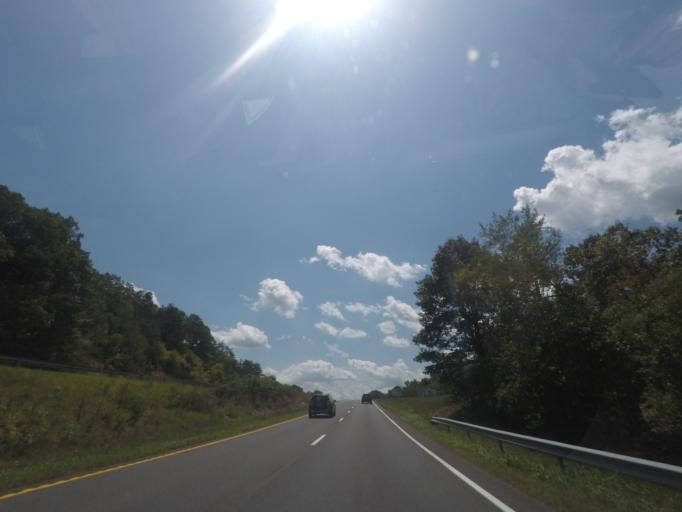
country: US
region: Virginia
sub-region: City of Winchester
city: Winchester
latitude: 39.1174
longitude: -78.1183
